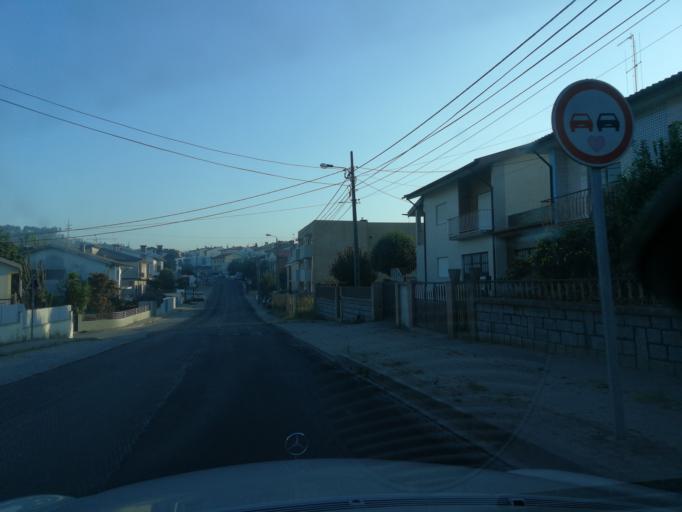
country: PT
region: Braga
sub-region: Braga
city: Braga
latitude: 41.5251
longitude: -8.4293
